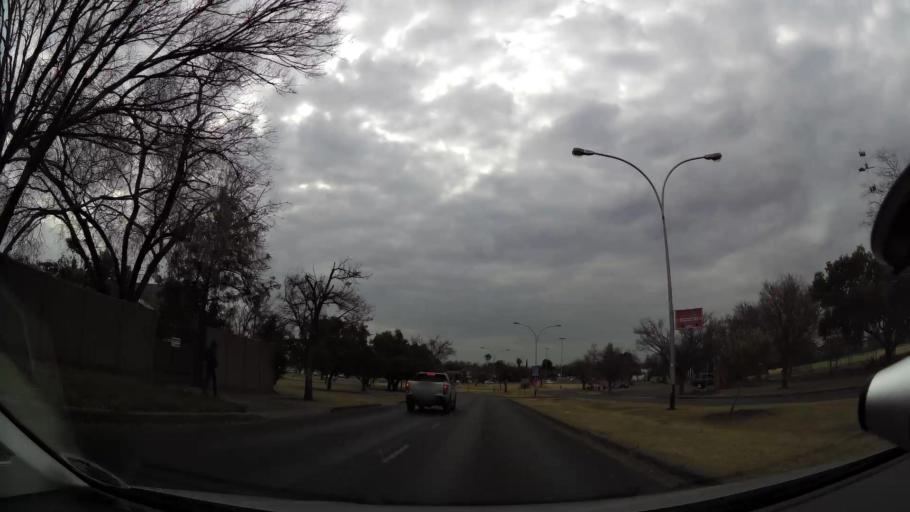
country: ZA
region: Orange Free State
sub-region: Mangaung Metropolitan Municipality
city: Bloemfontein
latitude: -29.0897
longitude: 26.2150
